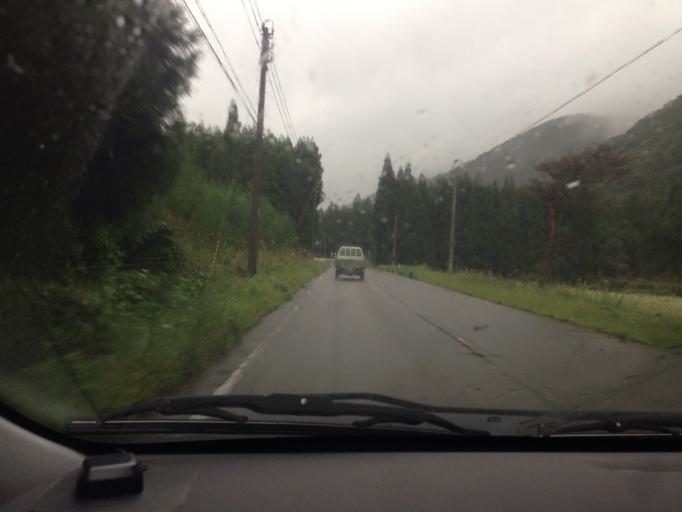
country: JP
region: Fukushima
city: Inawashiro
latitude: 37.3996
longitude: 140.1543
